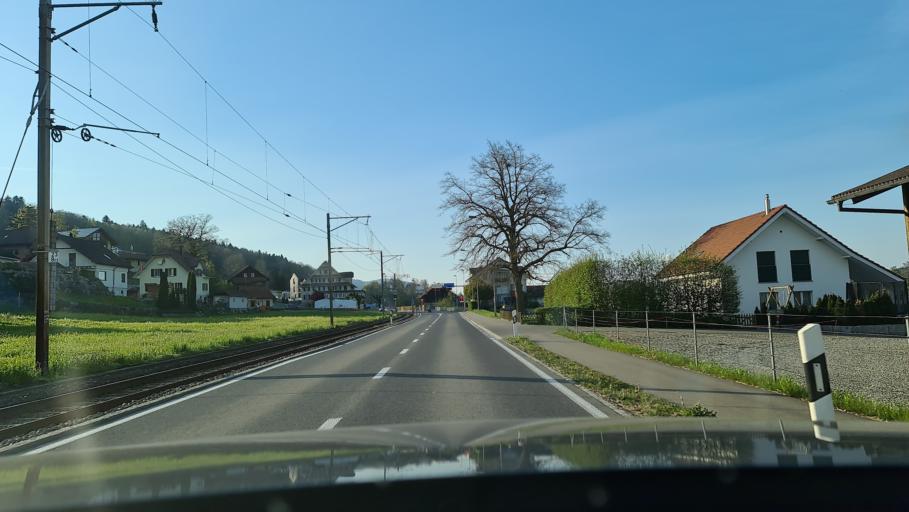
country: CH
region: Aargau
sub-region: Bezirk Kulm
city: Menziken
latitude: 47.2423
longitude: 8.2257
